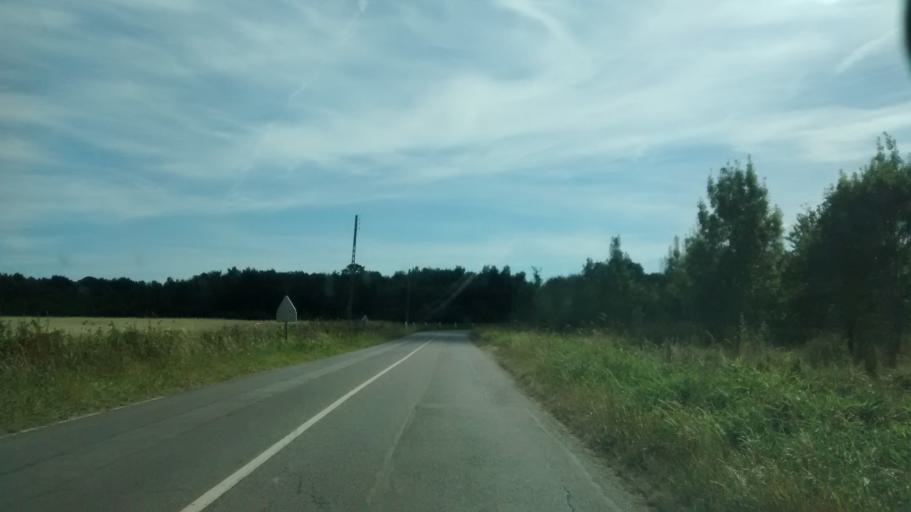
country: FR
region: Pays de la Loire
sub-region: Departement de la Loire-Atlantique
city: Pont-Saint-Martin
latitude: 47.1360
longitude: -1.6108
